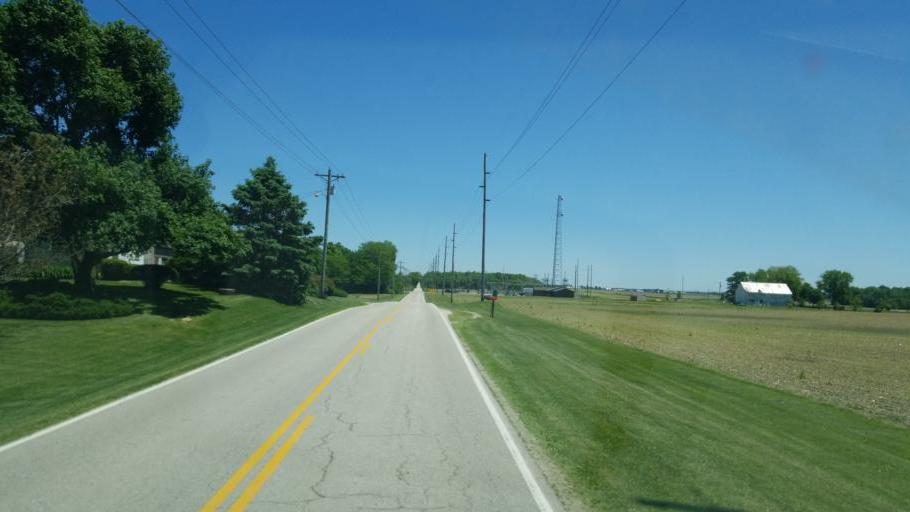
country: US
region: Ohio
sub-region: Darke County
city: Ansonia
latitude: 40.2648
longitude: -84.6407
